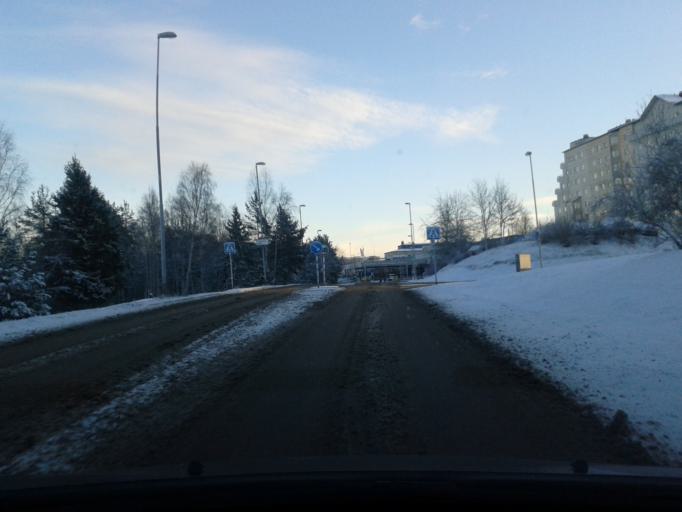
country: SE
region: Stockholm
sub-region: Haninge Kommun
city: Haninge
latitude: 59.1733
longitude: 18.1654
